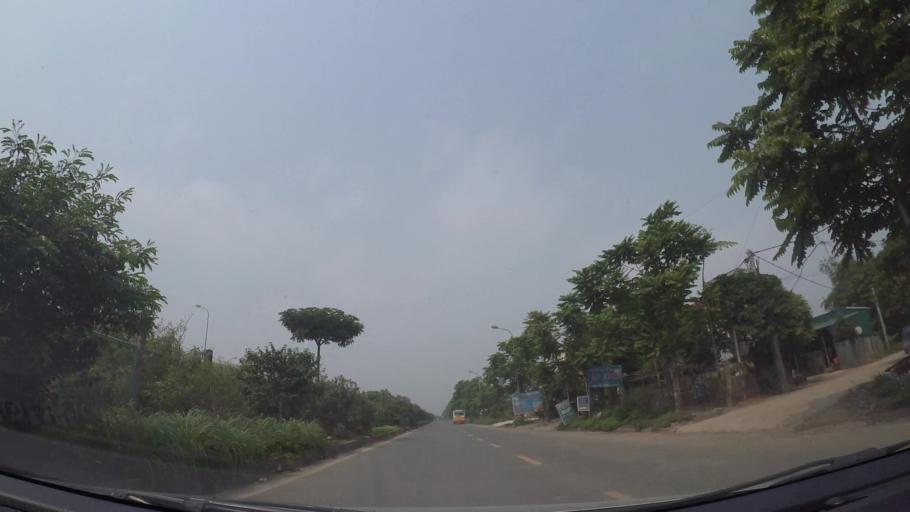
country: VN
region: Ha Noi
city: Quoc Oai
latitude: 20.9934
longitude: 105.5851
